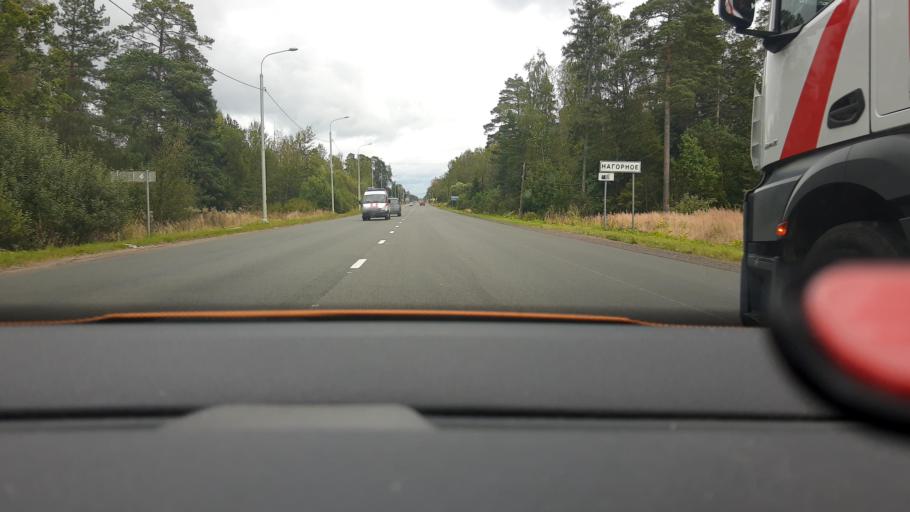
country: RU
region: Moskovskaya
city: Lesnoy
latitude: 56.0638
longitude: 38.0163
